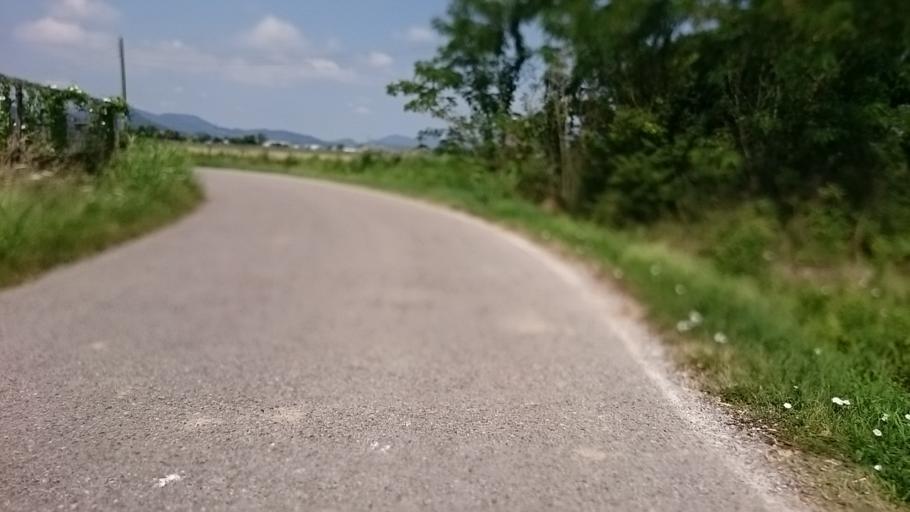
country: IT
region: Veneto
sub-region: Provincia di Padova
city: Terradura
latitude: 45.3309
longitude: 11.8338
